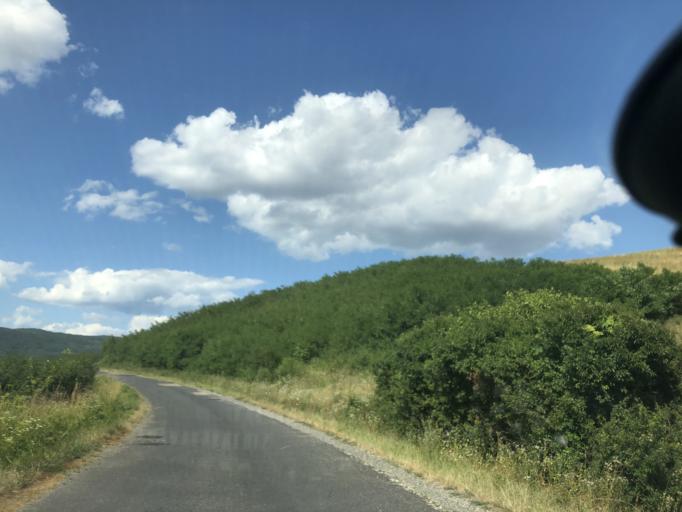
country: HU
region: Borsod-Abauj-Zemplen
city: Szendro
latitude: 48.5438
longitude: 20.7983
